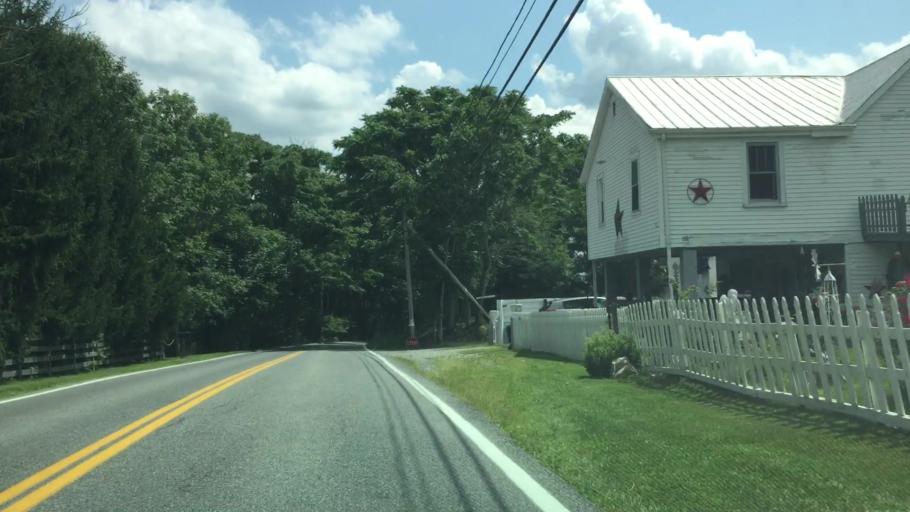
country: US
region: Virginia
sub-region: Pulaski County
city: Pulaski
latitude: 37.0155
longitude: -80.7355
